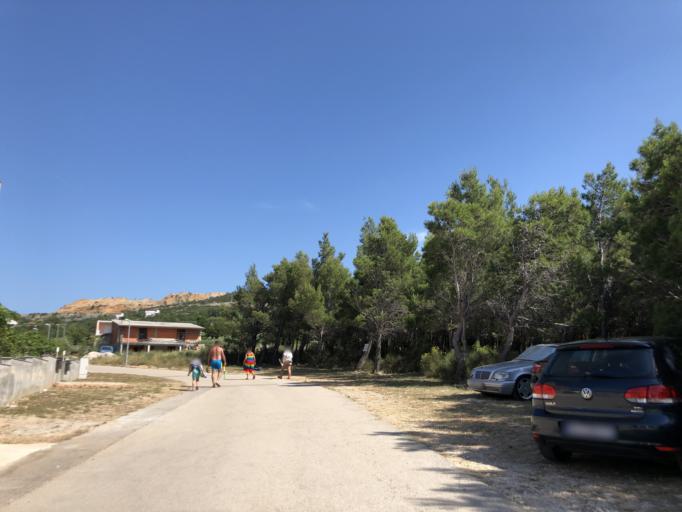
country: HR
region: Zadarska
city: Posedarje
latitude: 44.2458
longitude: 15.5357
